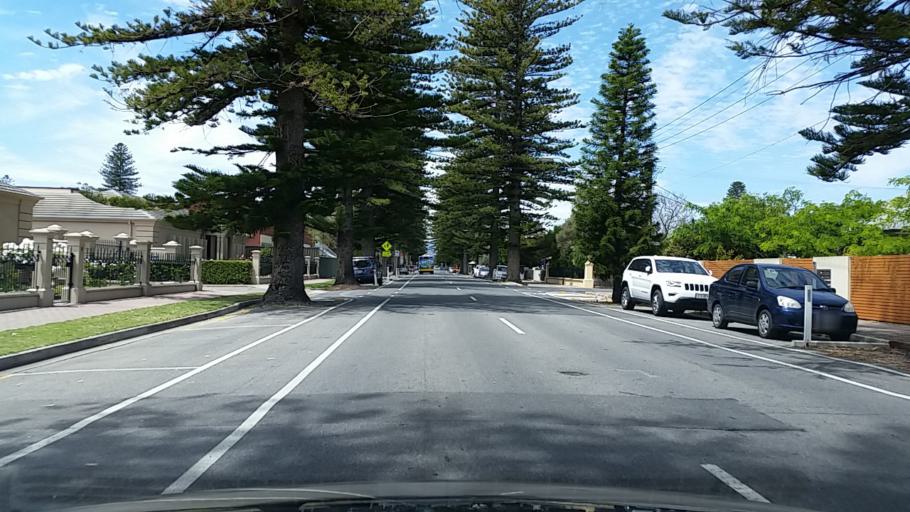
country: AU
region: South Australia
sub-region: Adelaide
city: Glenelg
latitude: -34.9852
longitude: 138.5155
